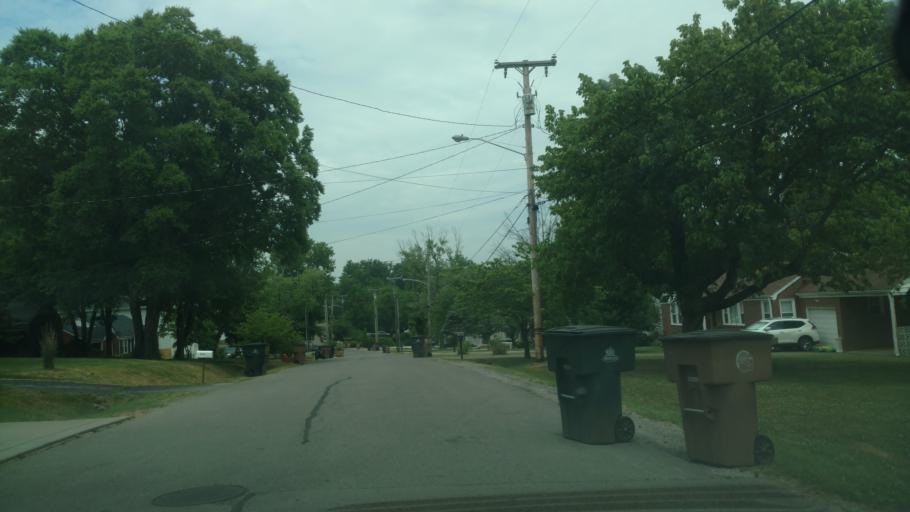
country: US
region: Tennessee
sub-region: Davidson County
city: Nashville
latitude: 36.1984
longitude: -86.7203
